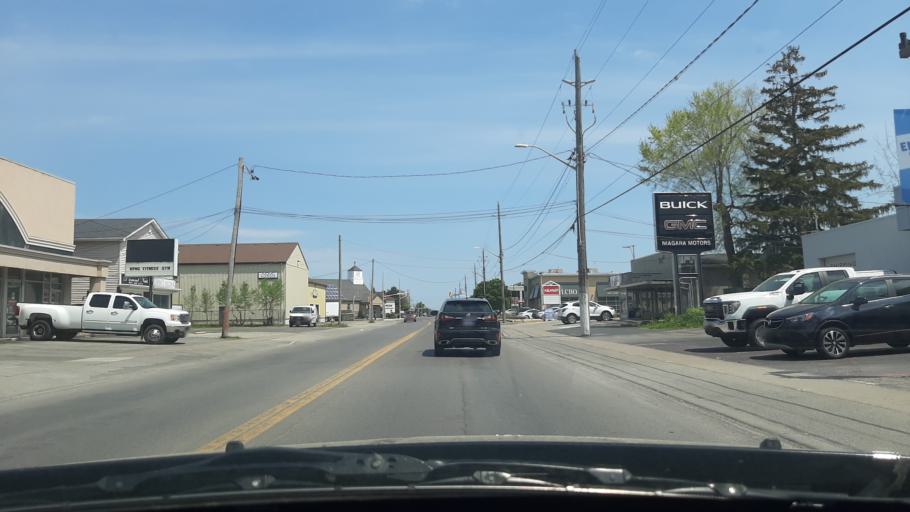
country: US
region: New York
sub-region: Niagara County
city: Youngstown
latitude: 43.2228
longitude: -79.1210
